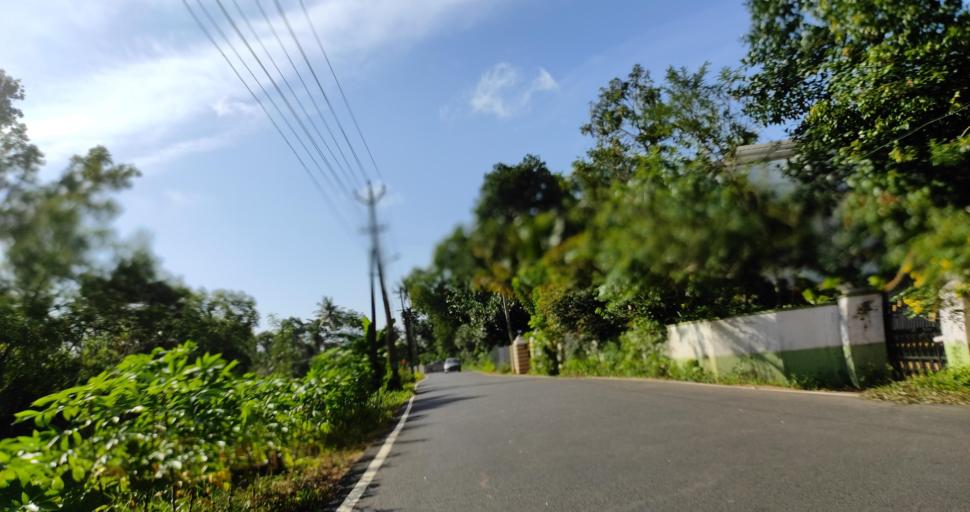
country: IN
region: Kerala
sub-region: Alappuzha
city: Shertallai
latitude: 9.6141
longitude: 76.3318
